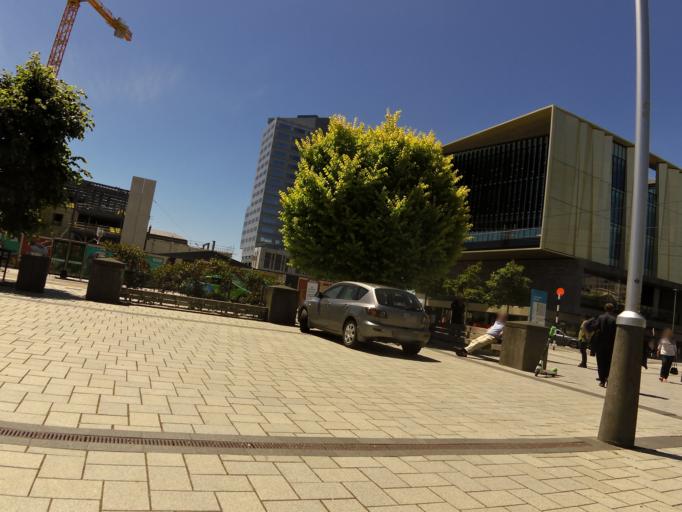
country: NZ
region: Canterbury
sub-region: Christchurch City
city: Christchurch
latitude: -43.5305
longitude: 172.6362
